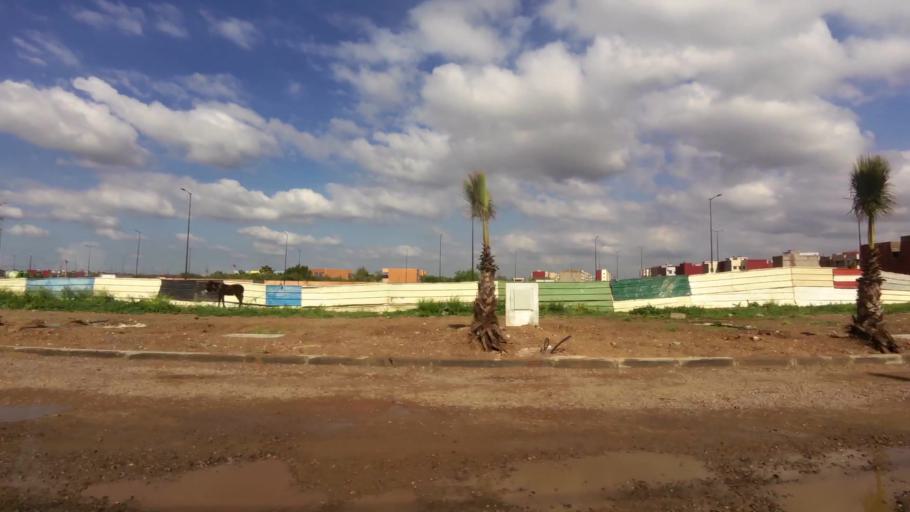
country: MA
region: Chaouia-Ouardigha
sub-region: Settat Province
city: Berrechid
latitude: 33.2647
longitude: -7.5714
